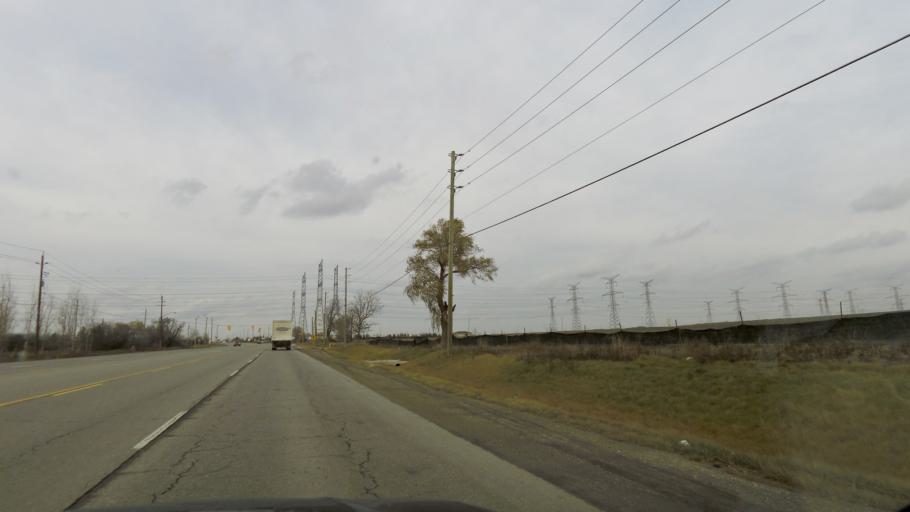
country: CA
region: Ontario
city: Etobicoke
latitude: 43.7563
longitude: -79.6425
